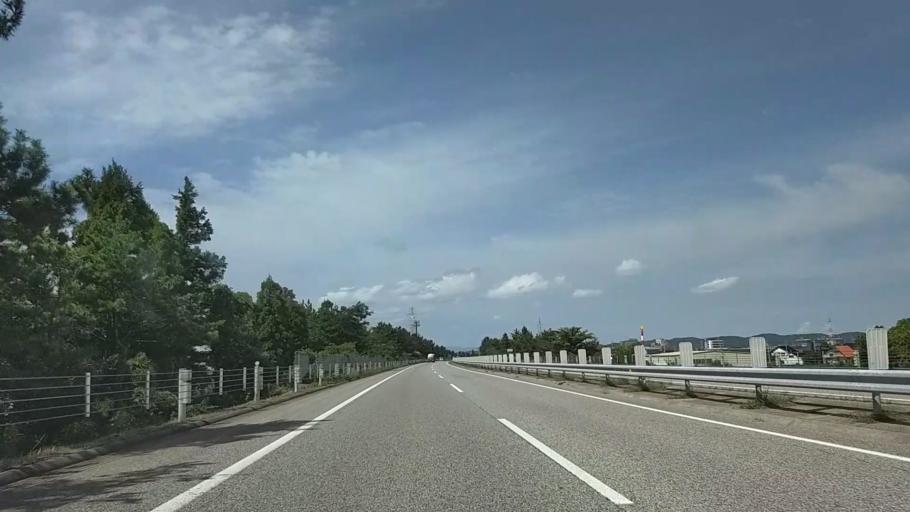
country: JP
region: Toyama
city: Toyama-shi
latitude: 36.6479
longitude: 137.2212
